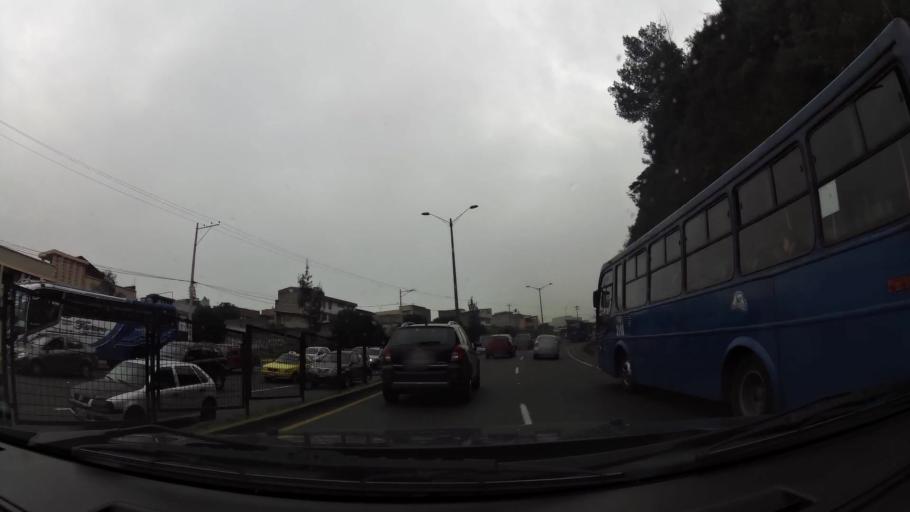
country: EC
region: Pichincha
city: Quito
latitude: -0.2267
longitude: -78.4899
